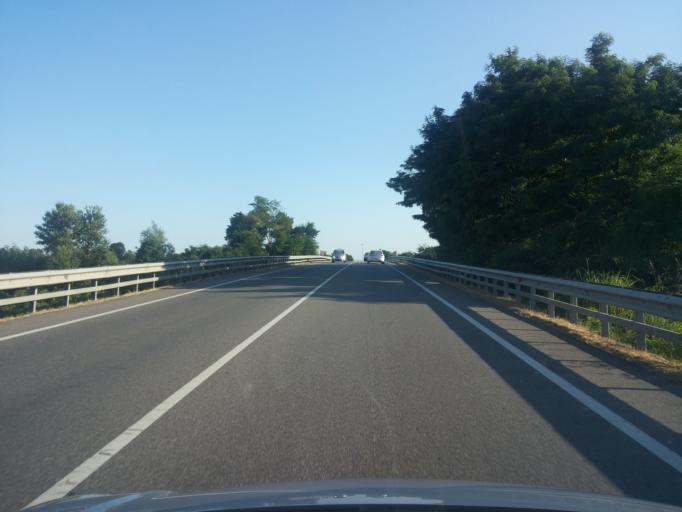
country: IT
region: Piedmont
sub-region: Provincia di Vercelli
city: Caresanablot
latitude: 45.3296
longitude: 8.3899
